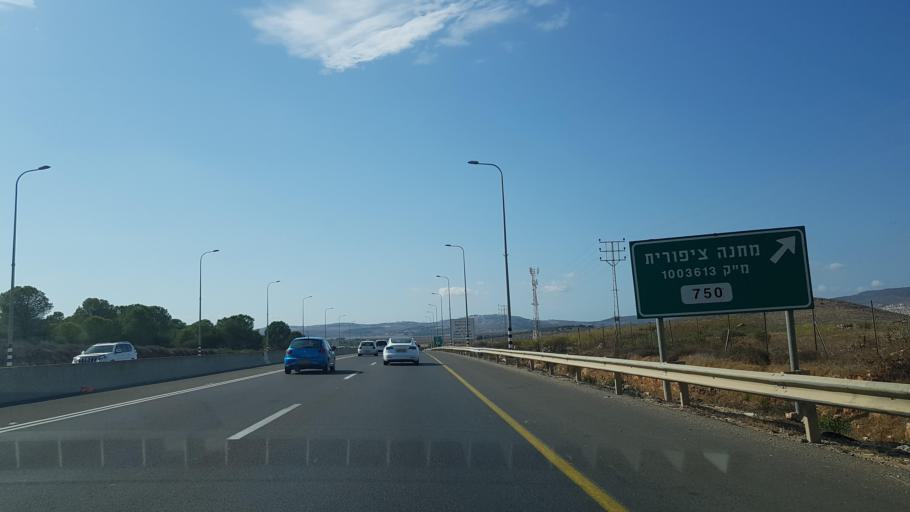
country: IL
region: Northern District
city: Rumat Heib
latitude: 32.7687
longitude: 35.3054
